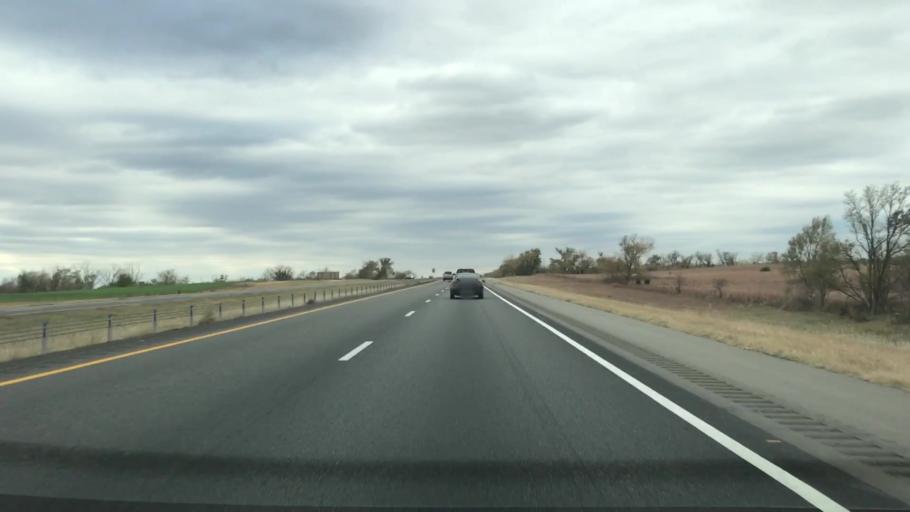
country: US
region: Oklahoma
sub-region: Beckham County
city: Elk City
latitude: 35.3858
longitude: -99.4874
